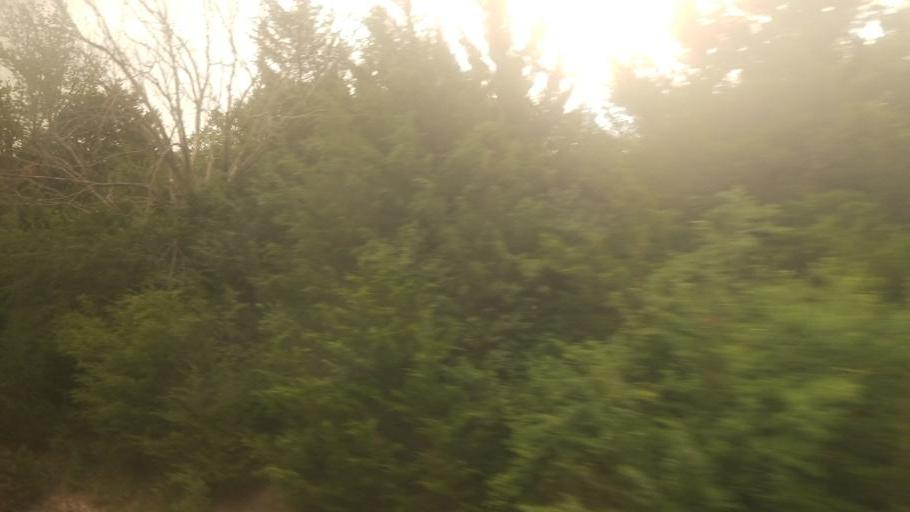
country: US
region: Kansas
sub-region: Shawnee County
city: Topeka
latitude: 39.0174
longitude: -95.6777
